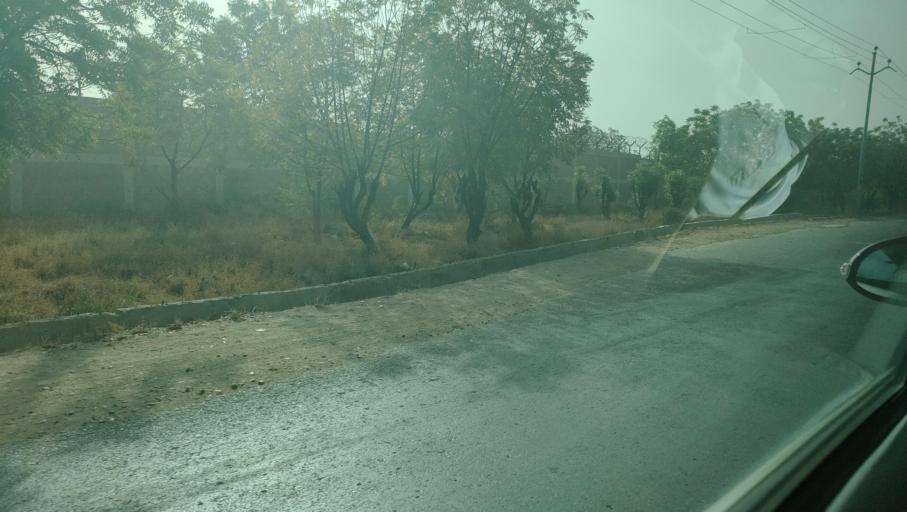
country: PK
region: Sindh
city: Malir Cantonment
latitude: 24.9269
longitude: 67.1798
